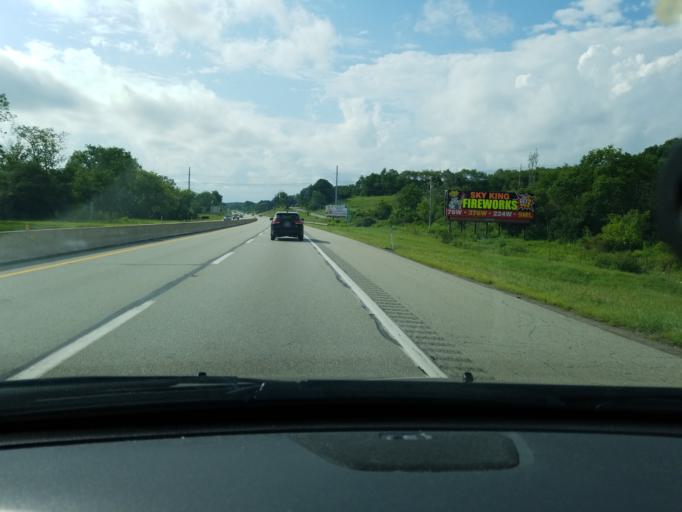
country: US
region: Pennsylvania
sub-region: Butler County
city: Fernway
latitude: 40.7073
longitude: -80.1245
